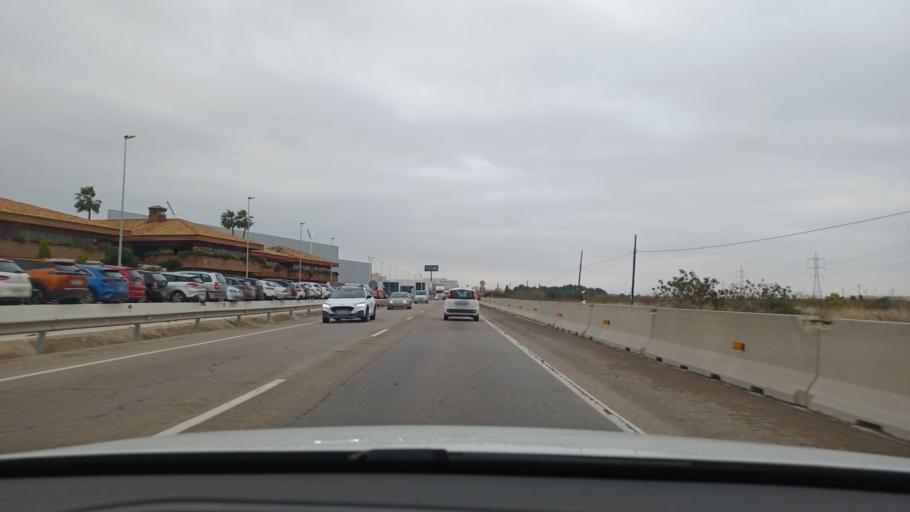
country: ES
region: Valencia
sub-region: Provincia de Castello
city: Vila-real
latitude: 39.9187
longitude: -0.1095
